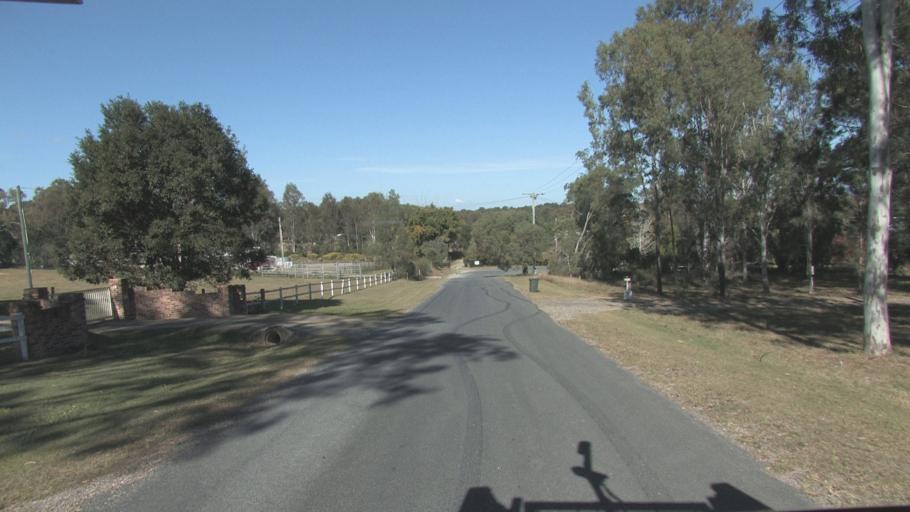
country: AU
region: Queensland
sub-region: Logan
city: Chambers Flat
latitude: -27.7802
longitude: 153.1408
